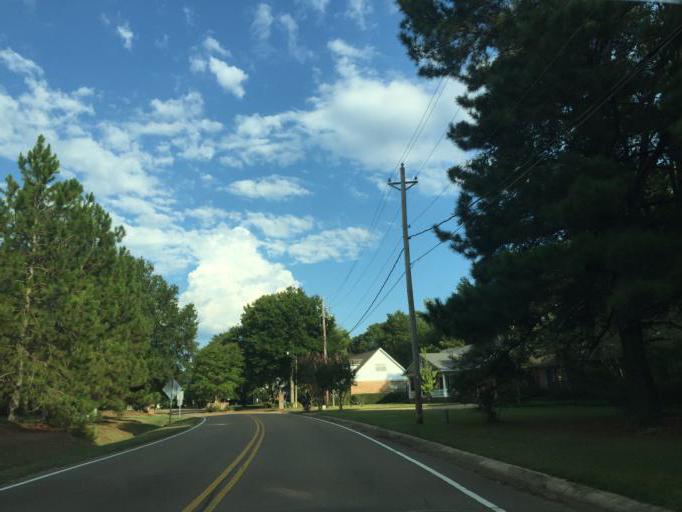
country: US
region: Mississippi
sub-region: Madison County
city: Ridgeland
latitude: 32.4292
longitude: -90.0989
